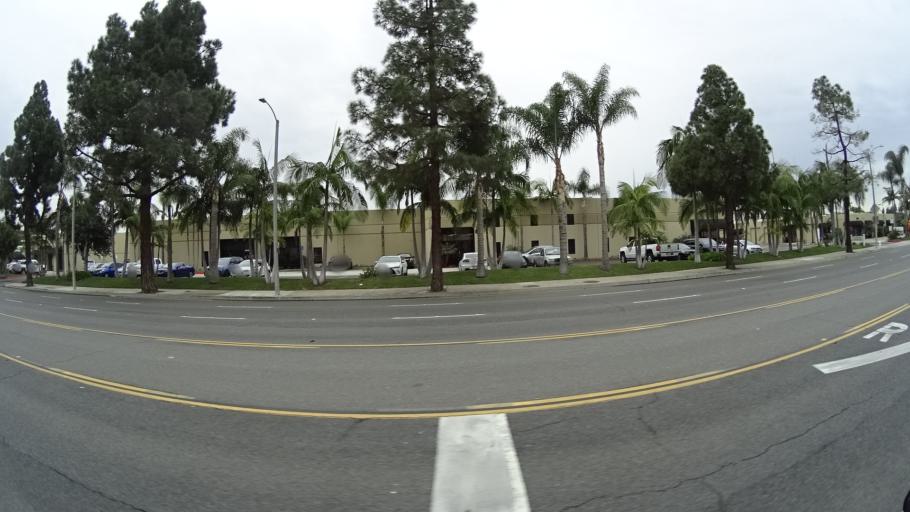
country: US
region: California
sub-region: Orange County
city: Fountain Valley
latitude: 33.7021
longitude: -117.9141
